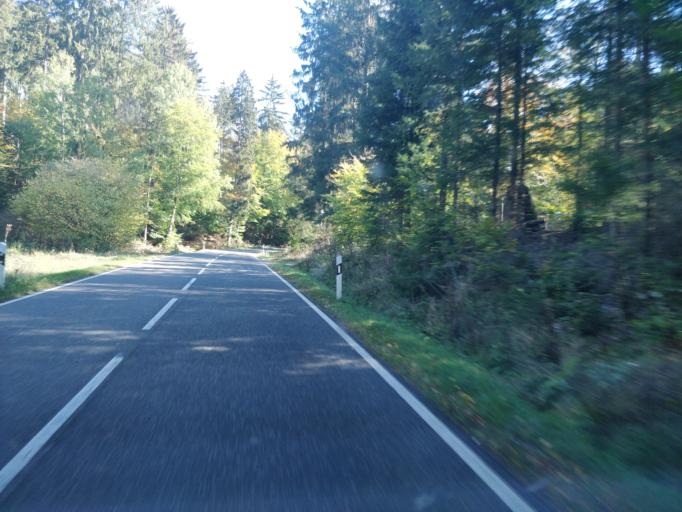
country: DE
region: North Rhine-Westphalia
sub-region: Regierungsbezirk Koln
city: Bad Munstereifel
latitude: 50.5475
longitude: 6.8090
